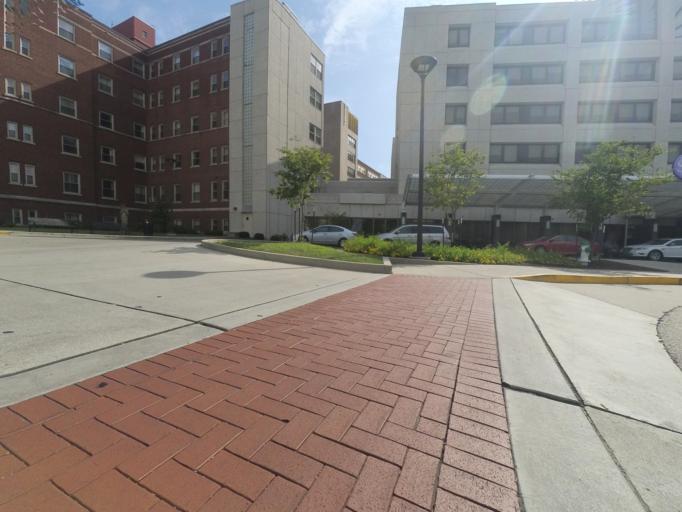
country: US
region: West Virginia
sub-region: Cabell County
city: Huntington
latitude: 38.4319
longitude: -82.4014
